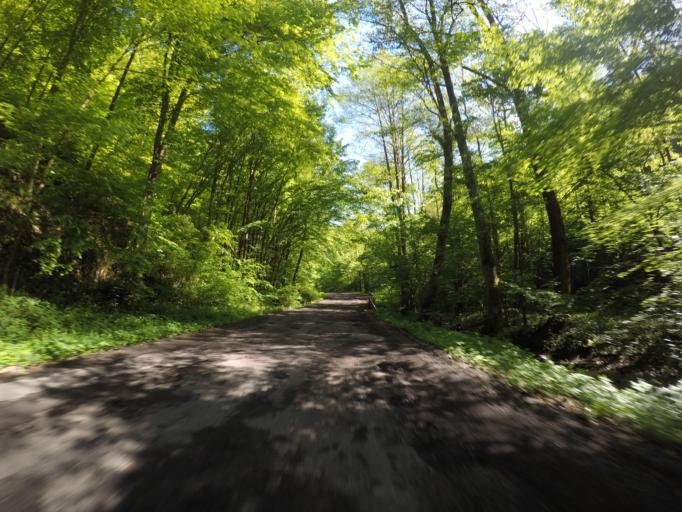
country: SK
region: Banskobystricky
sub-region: Okres Banska Bystrica
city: Zvolen
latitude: 48.5802
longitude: 19.0043
